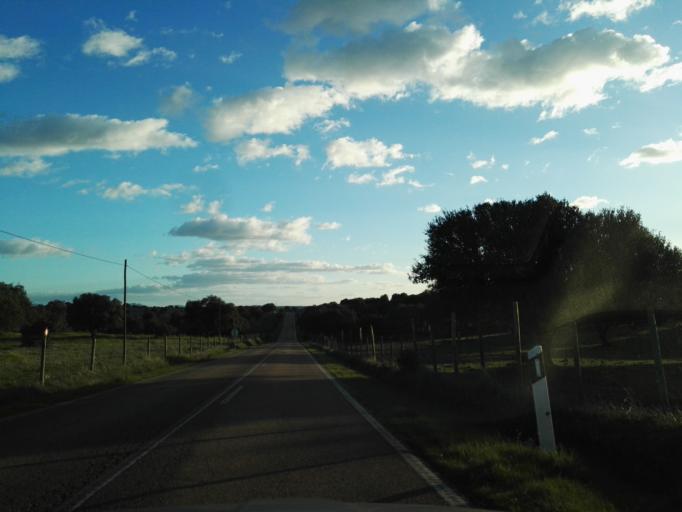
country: PT
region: Portalegre
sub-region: Elvas
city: Elvas
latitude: 38.8175
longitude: -7.1666
